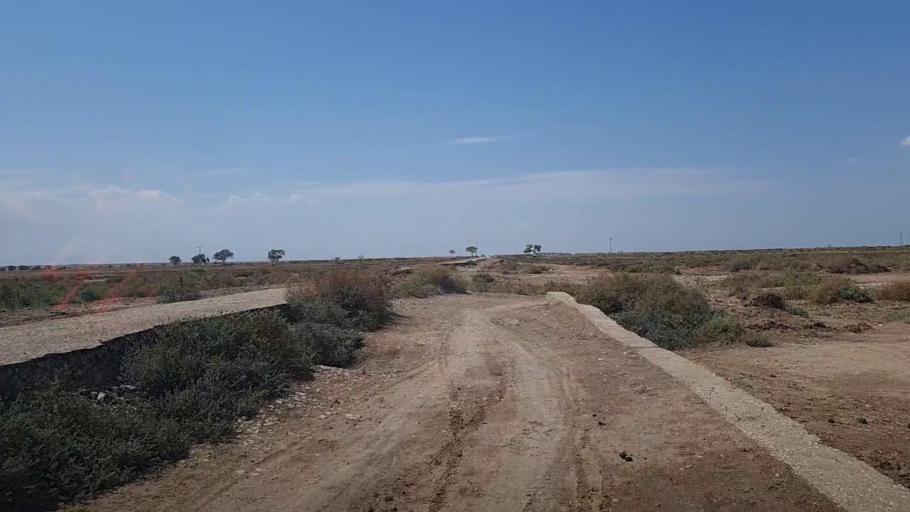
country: PK
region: Sindh
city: Sehwan
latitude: 26.3579
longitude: 67.6698
